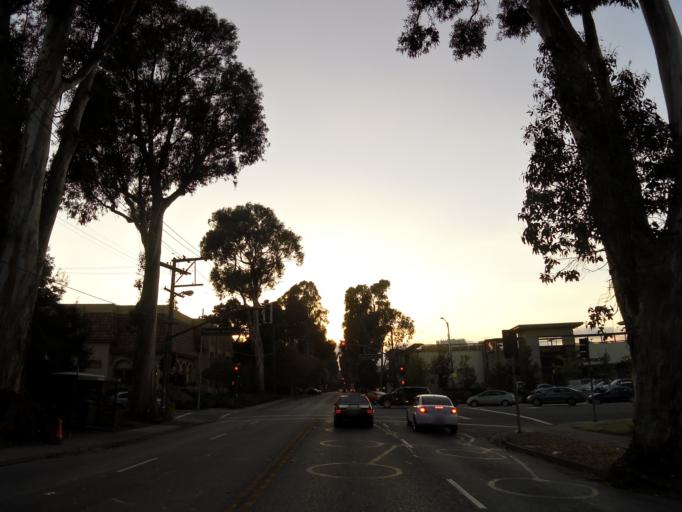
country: US
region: California
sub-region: San Mateo County
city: Burlingame
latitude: 37.5757
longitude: -122.3473
